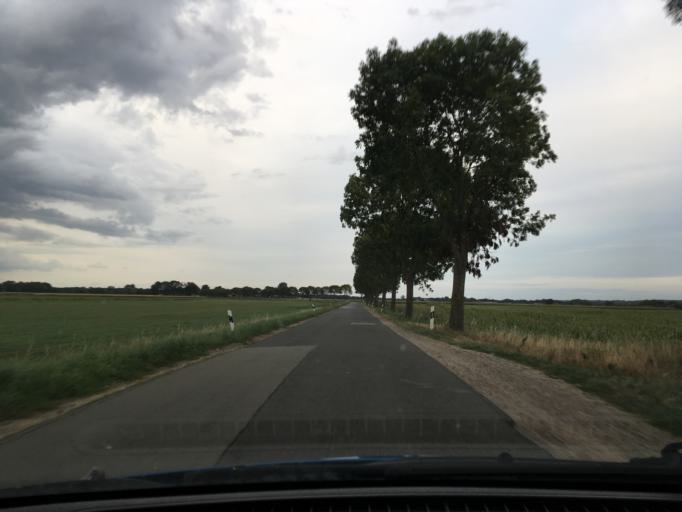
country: DE
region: Schleswig-Holstein
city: Lanze
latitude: 53.3770
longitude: 10.5919
